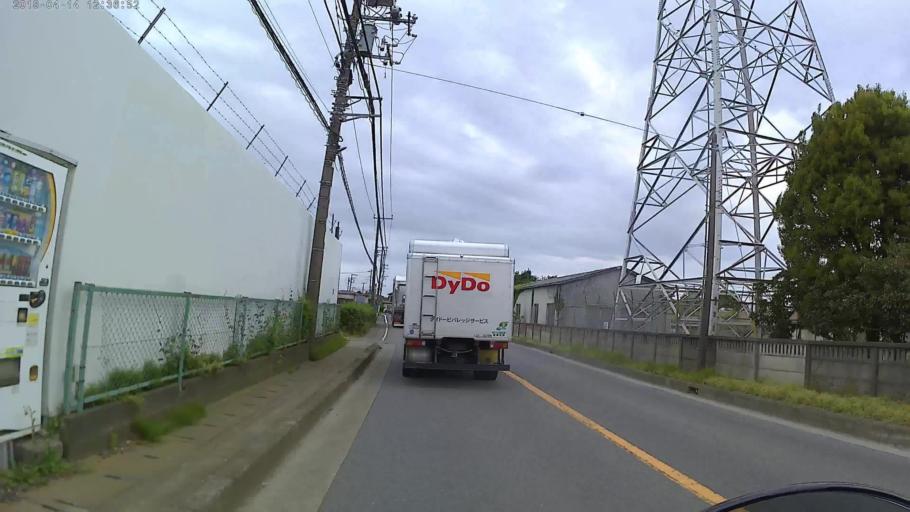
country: JP
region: Kanagawa
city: Atsugi
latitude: 35.4140
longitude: 139.4069
